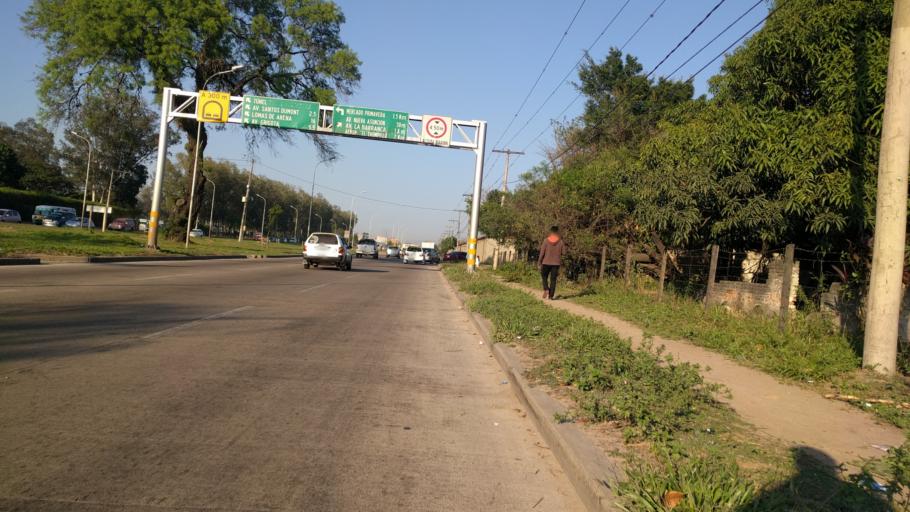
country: BO
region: Santa Cruz
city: Santa Cruz de la Sierra
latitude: -17.8126
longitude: -63.1629
